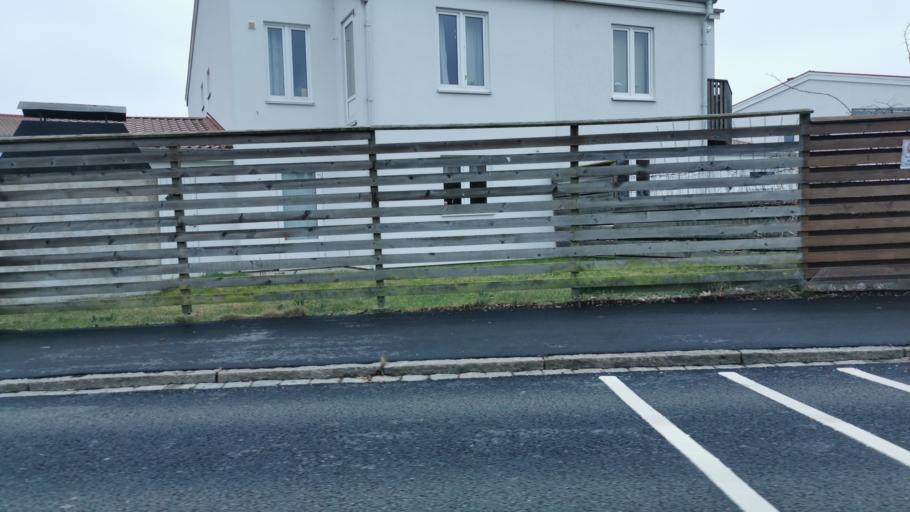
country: SE
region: Skane
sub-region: Burlovs Kommun
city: Arloev
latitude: 55.5898
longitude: 13.0812
